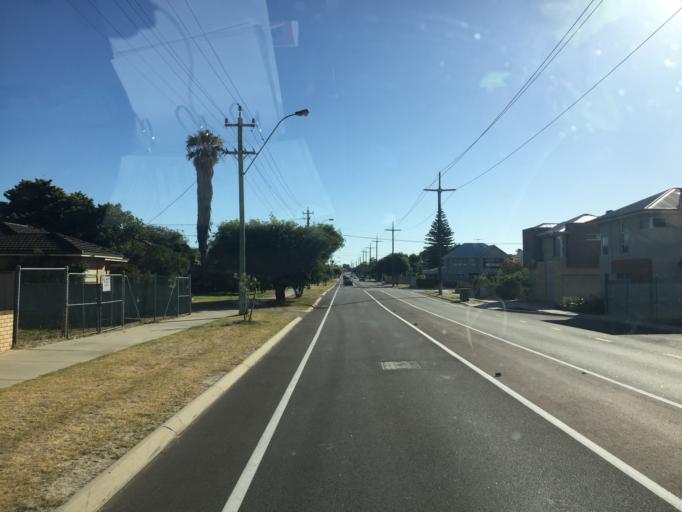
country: AU
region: Western Australia
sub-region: Belmont
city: Rivervale
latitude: -31.9629
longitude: 115.9263
